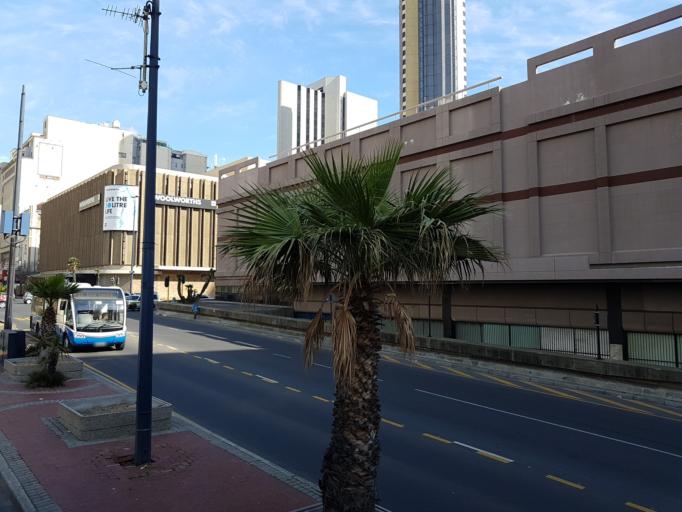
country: ZA
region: Western Cape
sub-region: City of Cape Town
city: Cape Town
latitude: -33.9216
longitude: 18.4238
